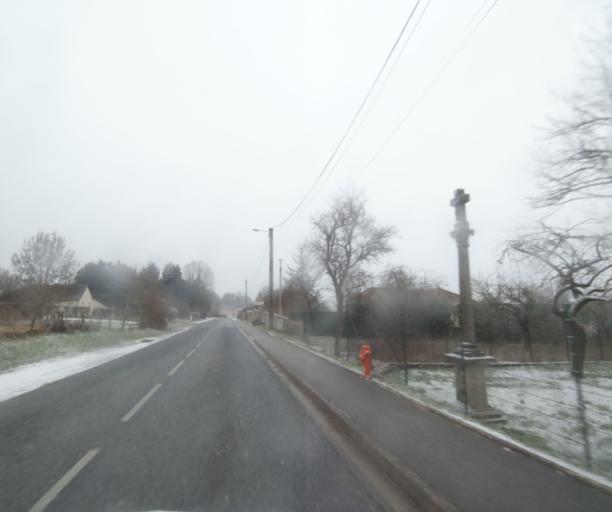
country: FR
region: Champagne-Ardenne
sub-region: Departement de la Haute-Marne
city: Wassy
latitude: 48.4998
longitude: 4.9582
